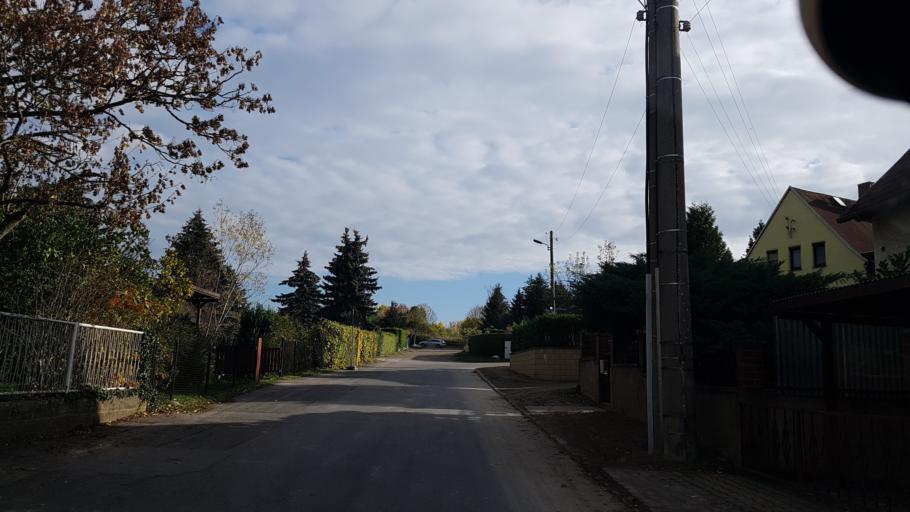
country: DE
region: Saxony
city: Oschatz
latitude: 51.2980
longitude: 13.1194
